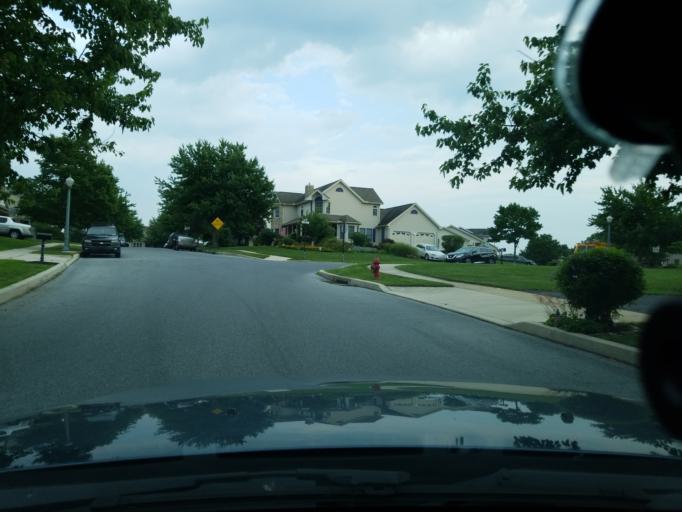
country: US
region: Pennsylvania
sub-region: Dauphin County
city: Hummelstown
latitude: 40.2694
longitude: -76.7240
